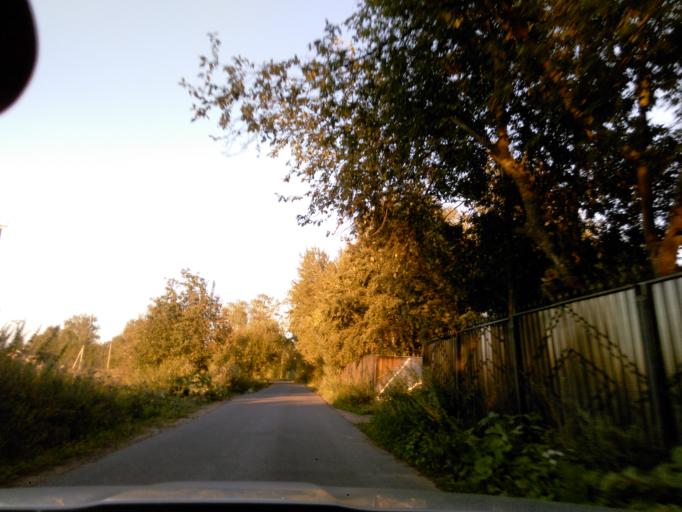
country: RU
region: Moskovskaya
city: Solnechnogorsk
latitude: 56.1282
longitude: 36.8453
